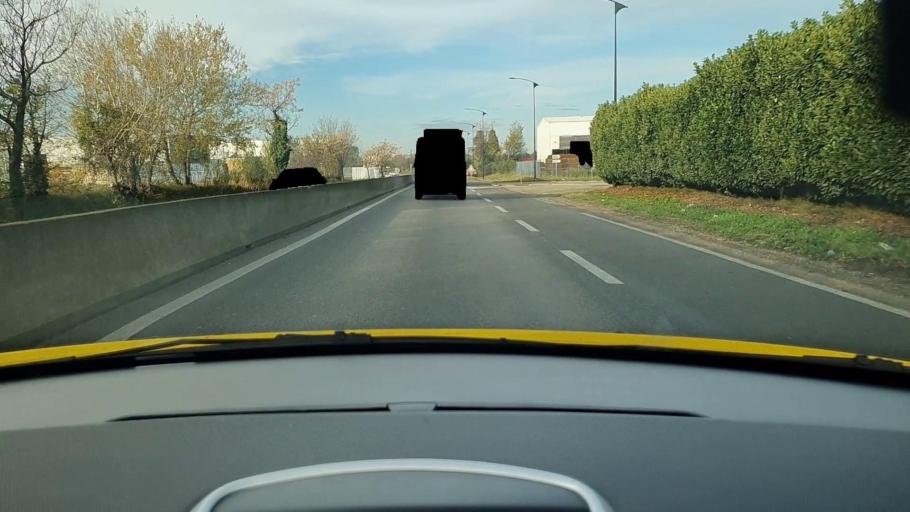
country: FR
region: Languedoc-Roussillon
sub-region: Departement du Gard
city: Beaucaire
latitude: 43.7905
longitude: 4.6389
